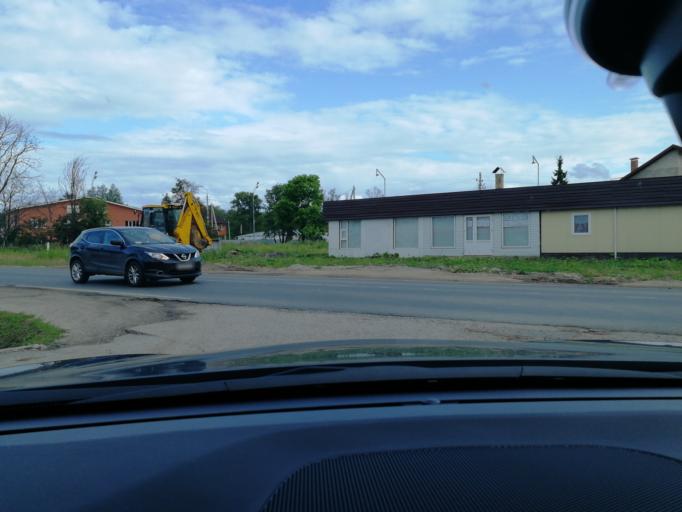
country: RU
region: Moskovskaya
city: Proletarskiy
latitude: 55.0313
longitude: 37.4268
